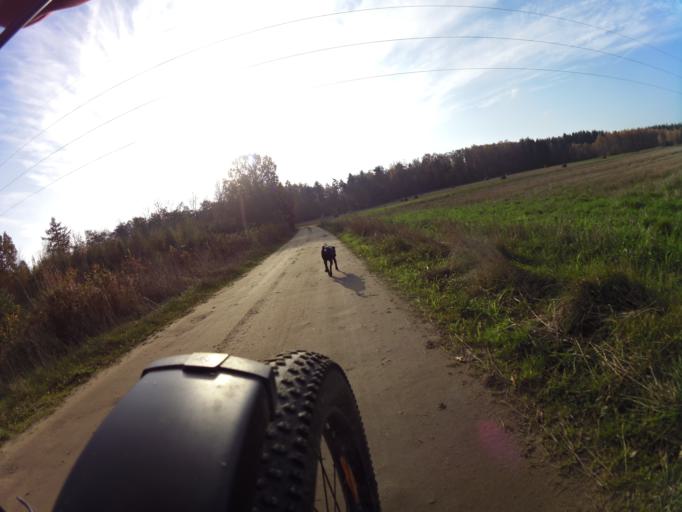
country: PL
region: Pomeranian Voivodeship
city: Strzelno
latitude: 54.7440
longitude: 18.2850
